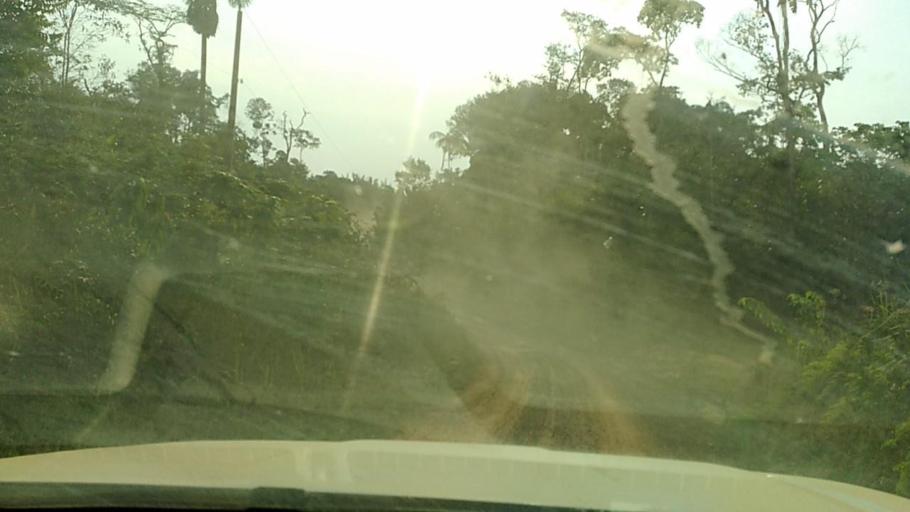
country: BR
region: Rondonia
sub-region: Porto Velho
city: Porto Velho
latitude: -8.5648
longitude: -64.0290
